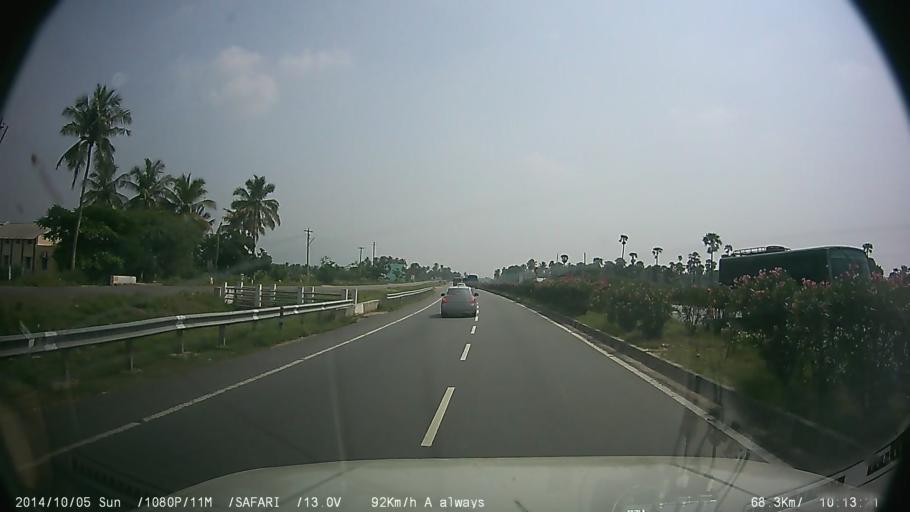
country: IN
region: Tamil Nadu
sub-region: Salem
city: Ilampillai
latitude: 11.5497
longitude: 77.9972
